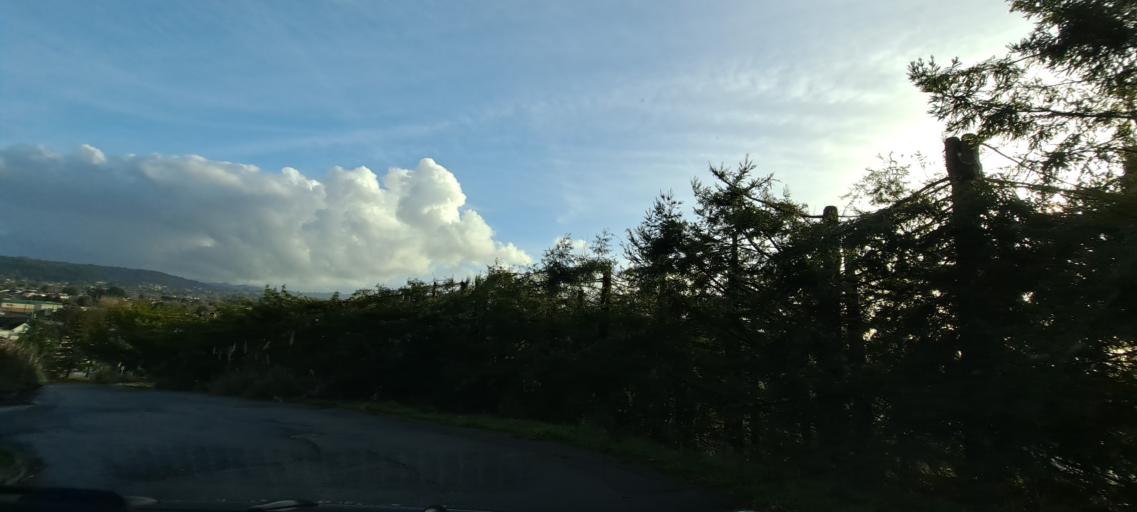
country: US
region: California
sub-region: Humboldt County
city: Fortuna
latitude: 40.5990
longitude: -124.1483
